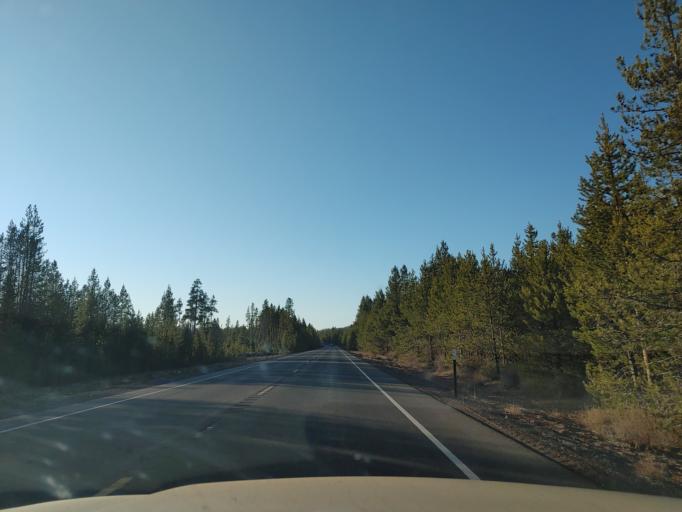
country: US
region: Oregon
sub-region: Deschutes County
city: La Pine
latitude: 43.4170
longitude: -121.8375
